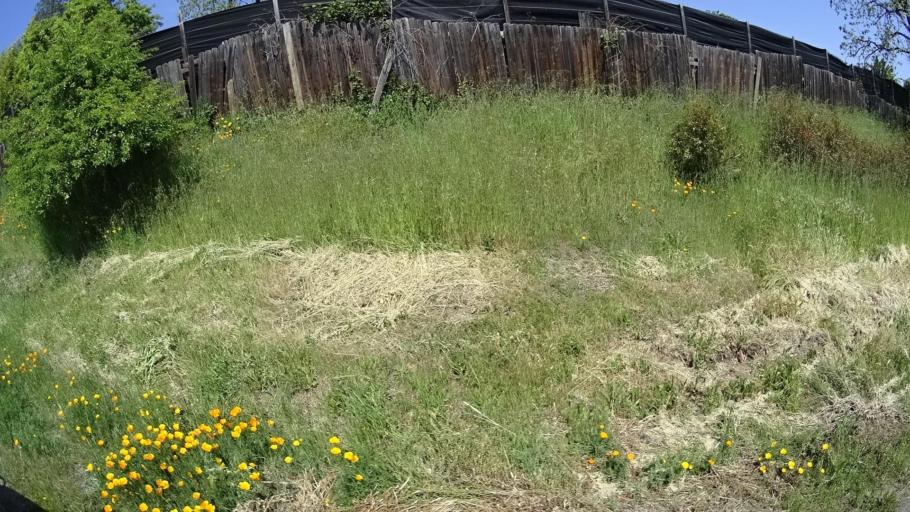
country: US
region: California
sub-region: Humboldt County
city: Redway
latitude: 40.2750
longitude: -123.6353
